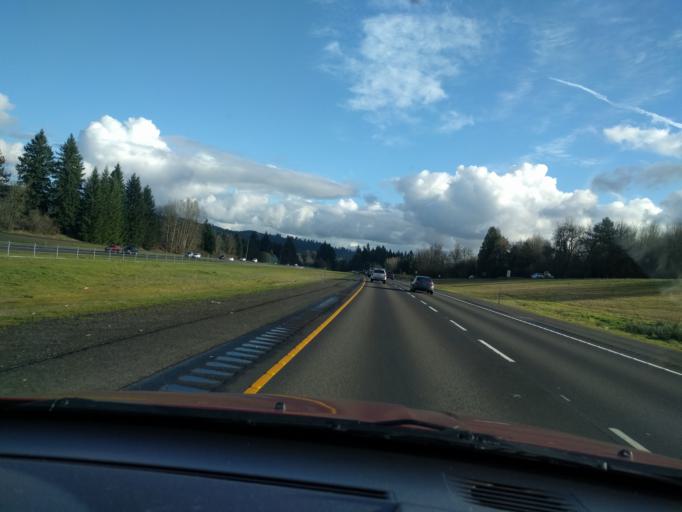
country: US
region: Oregon
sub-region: Clackamas County
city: Stafford
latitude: 45.3698
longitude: -122.7057
